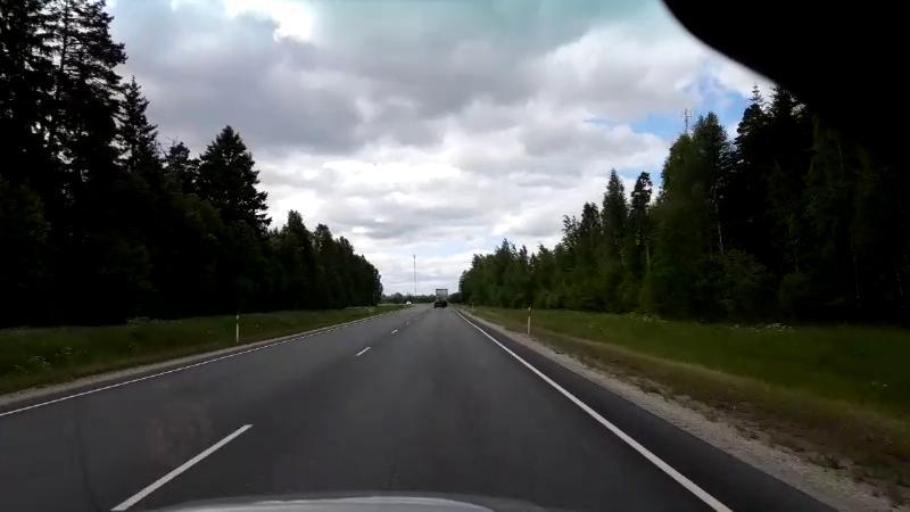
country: EE
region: Raplamaa
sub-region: Maerjamaa vald
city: Marjamaa
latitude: 58.7757
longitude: 24.4136
